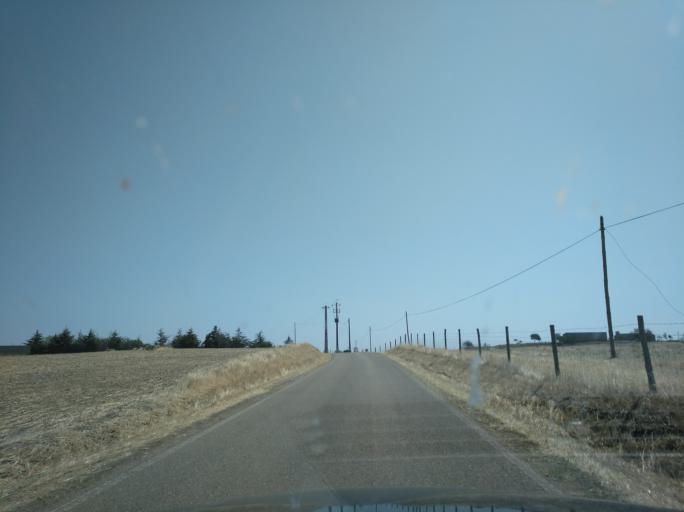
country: PT
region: Portalegre
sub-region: Campo Maior
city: Campo Maior
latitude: 39.0241
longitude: -7.0389
